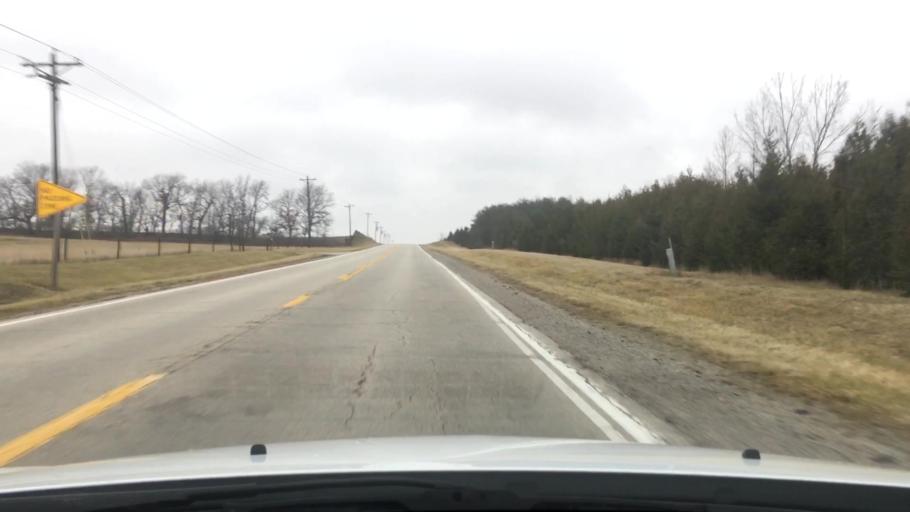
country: US
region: Illinois
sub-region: Iroquois County
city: Watseka
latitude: 40.8907
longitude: -87.6852
